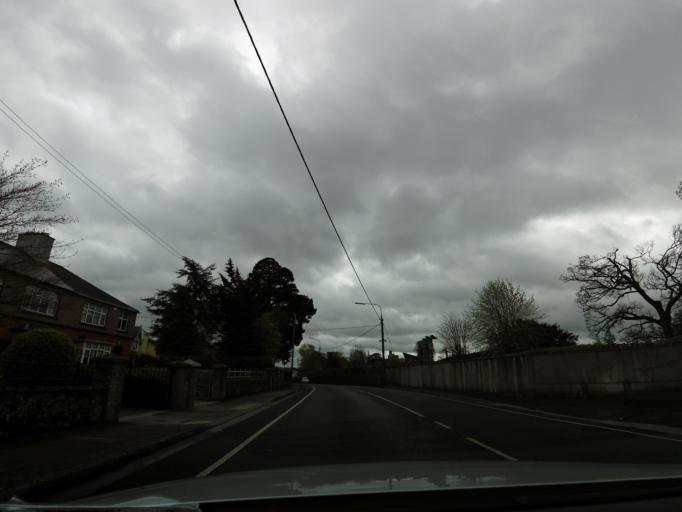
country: IE
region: Leinster
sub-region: Kilkenny
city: Kilkenny
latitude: 52.6603
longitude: -7.2595
